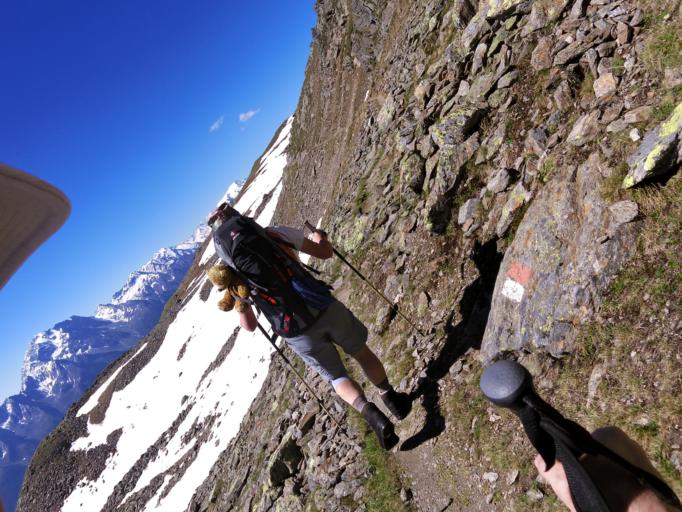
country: AT
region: Tyrol
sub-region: Politischer Bezirk Innsbruck Land
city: Neustift im Stubaital
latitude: 47.1419
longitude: 11.2623
